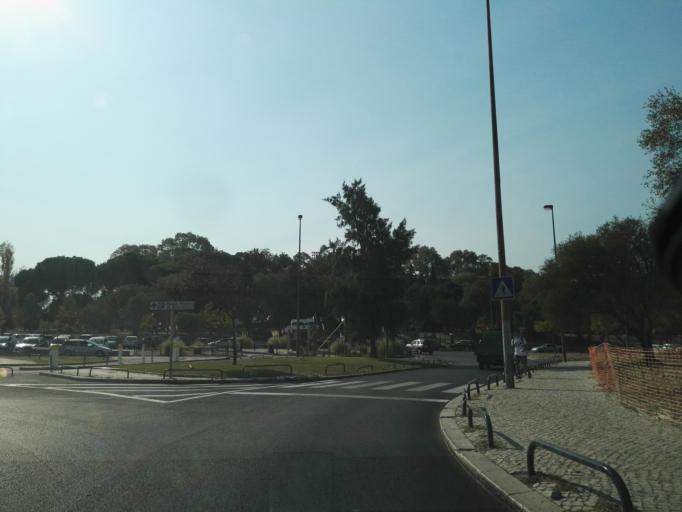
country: PT
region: Lisbon
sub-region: Odivelas
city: Olival do Basto
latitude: 38.7530
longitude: -9.1590
